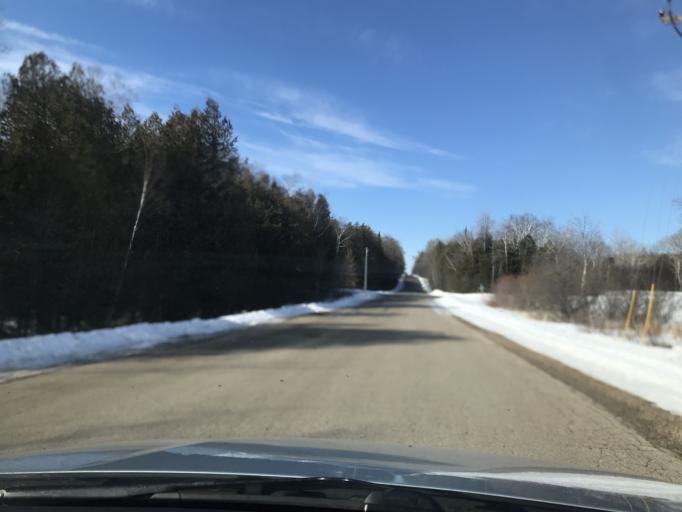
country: US
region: Wisconsin
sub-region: Oconto County
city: Gillett
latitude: 44.9616
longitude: -88.2738
